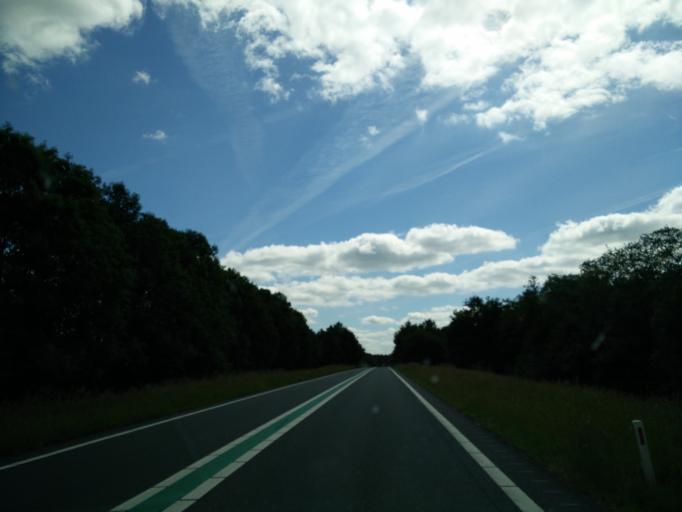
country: NL
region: Drenthe
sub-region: Gemeente Coevorden
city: Sleen
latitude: 52.8176
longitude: 6.6604
